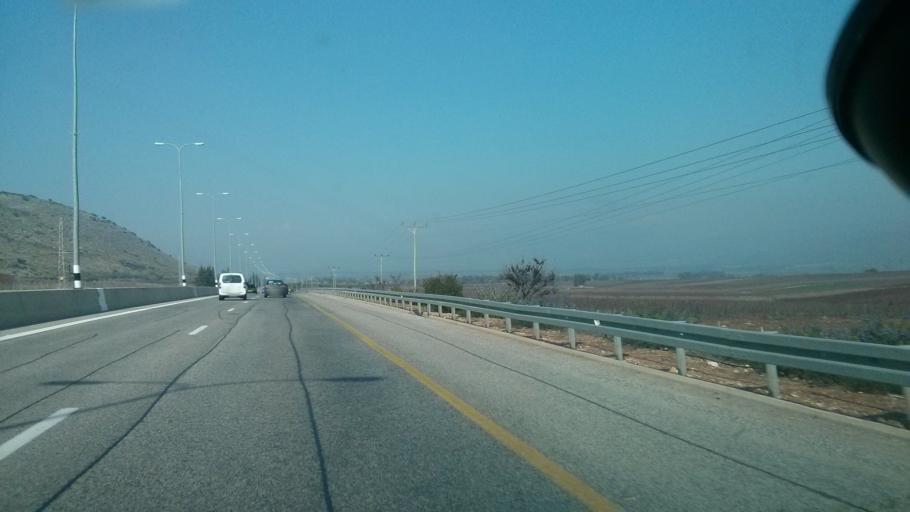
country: IL
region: Northern District
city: Rosh Pinna
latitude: 33.0563
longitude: 35.5737
